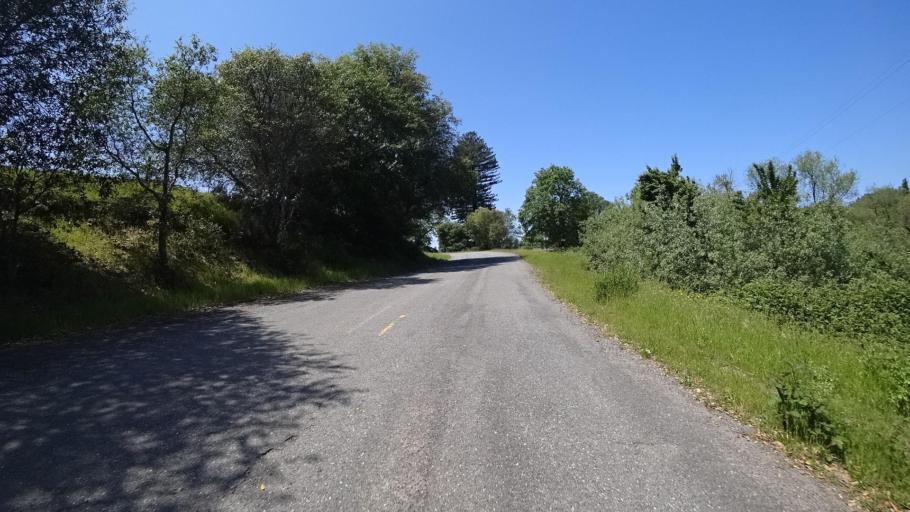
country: US
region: California
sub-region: Humboldt County
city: Redway
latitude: 40.2165
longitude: -123.6353
